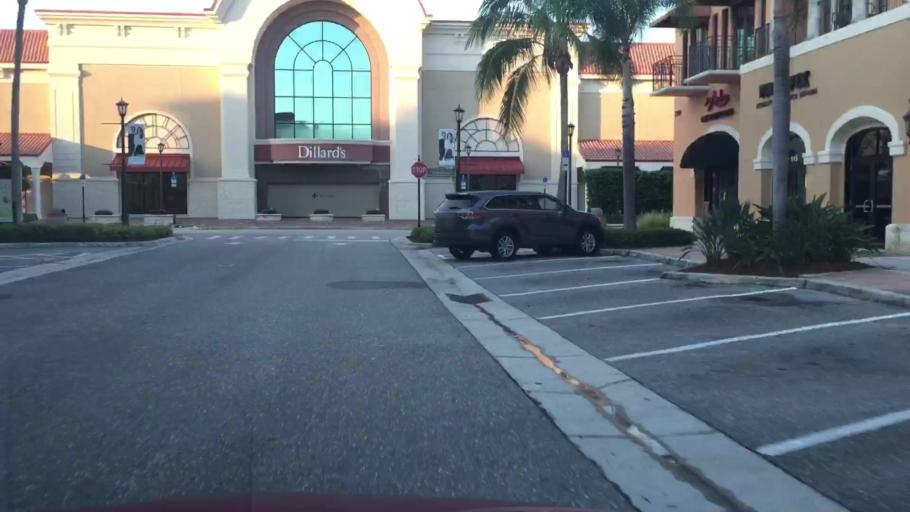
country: US
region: Florida
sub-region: Lee County
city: Estero
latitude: 26.4006
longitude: -81.8074
